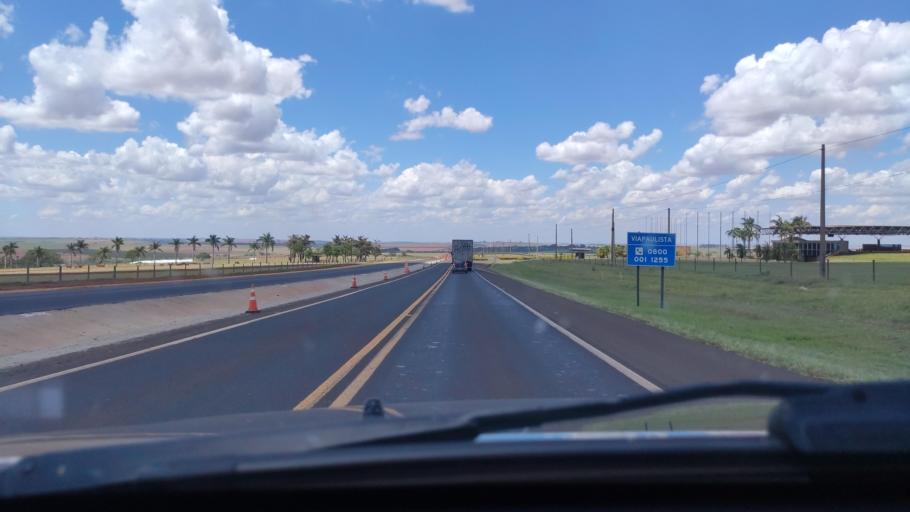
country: BR
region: Sao Paulo
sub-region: Jau
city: Jau
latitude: -22.1933
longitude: -48.5061
